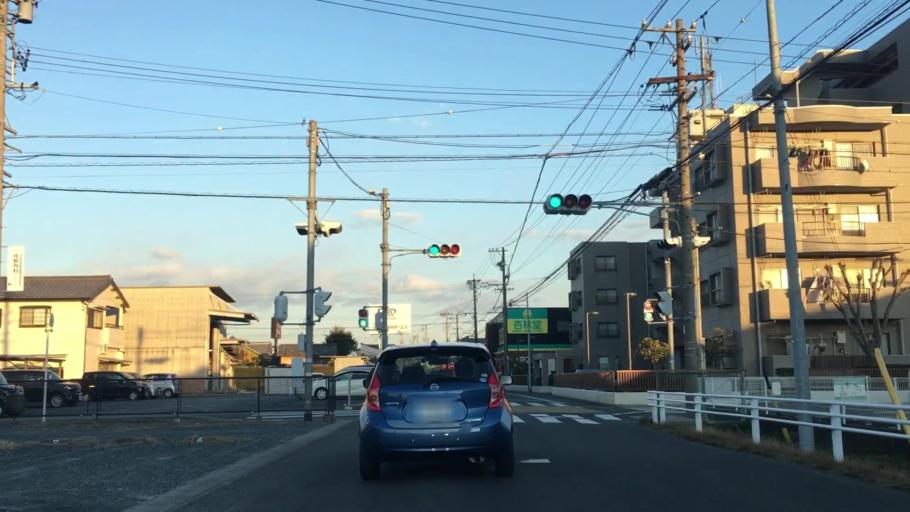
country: JP
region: Shizuoka
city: Hamamatsu
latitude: 34.7339
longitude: 137.7697
